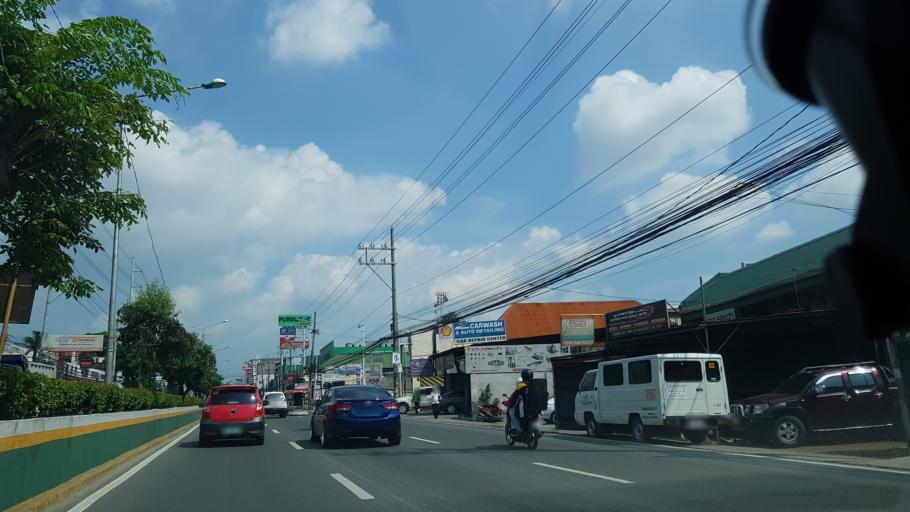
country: PH
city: Sambayanihan People's Village
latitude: 14.4672
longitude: 121.0147
